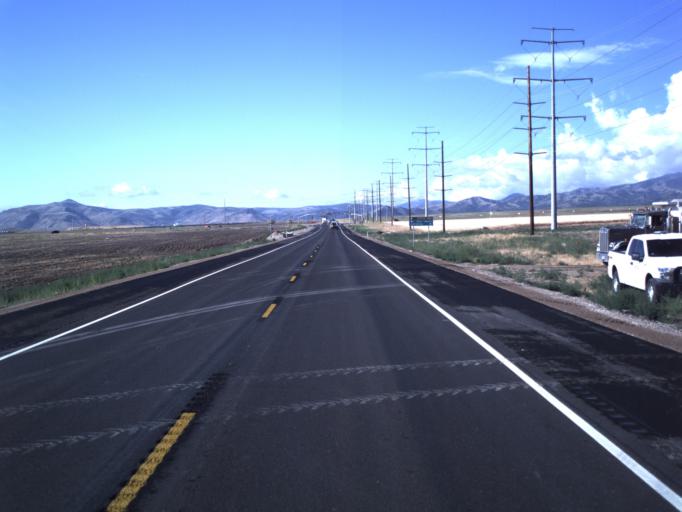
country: US
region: Utah
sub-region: Salt Lake County
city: Oquirrh
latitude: 40.5811
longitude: -112.0607
